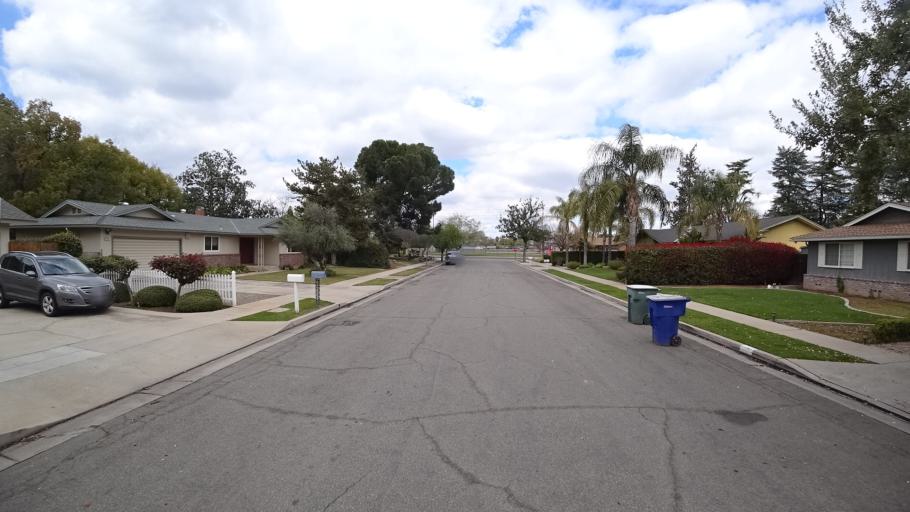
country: US
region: California
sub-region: Fresno County
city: Fresno
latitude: 36.8293
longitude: -119.8058
